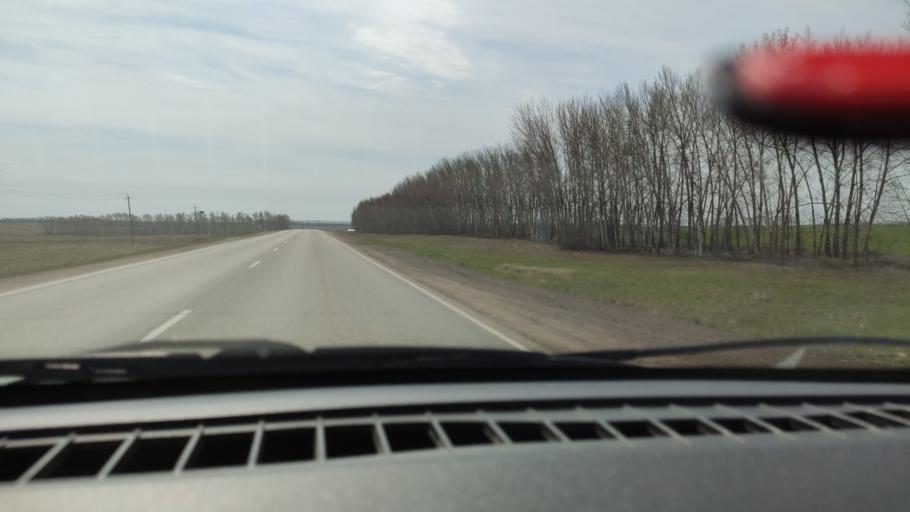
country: RU
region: Bashkortostan
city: Dyurtyuli
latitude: 55.4763
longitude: 54.7917
